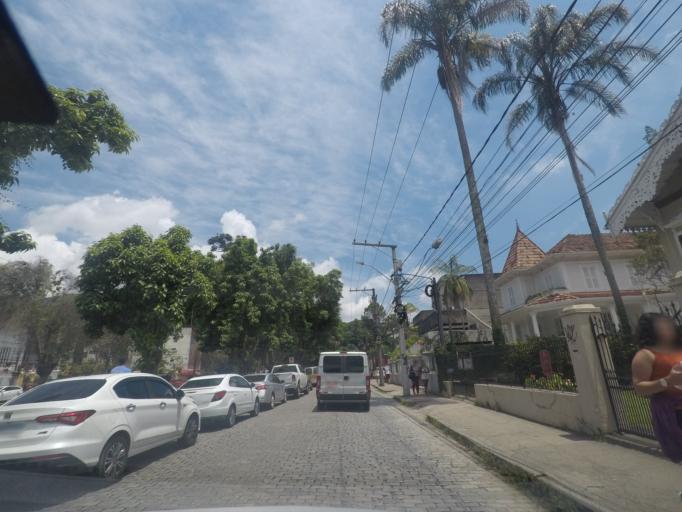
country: BR
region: Rio de Janeiro
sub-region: Petropolis
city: Petropolis
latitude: -22.5068
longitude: -43.1774
